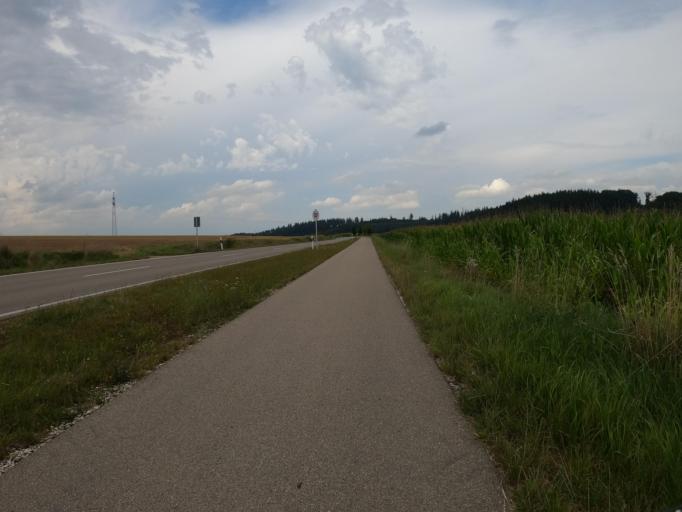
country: DE
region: Bavaria
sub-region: Swabia
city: Pfaffenhofen an der Roth
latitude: 48.3666
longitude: 10.2037
